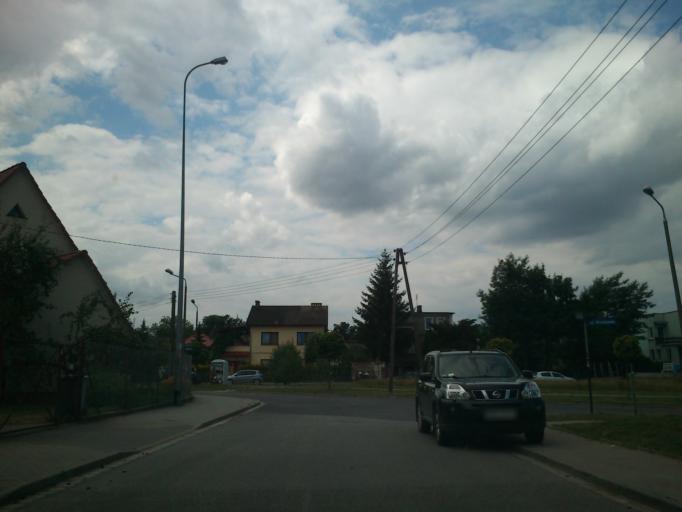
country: PL
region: Lower Silesian Voivodeship
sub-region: Powiat wroclawski
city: Smolec
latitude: 51.1584
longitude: 16.8972
